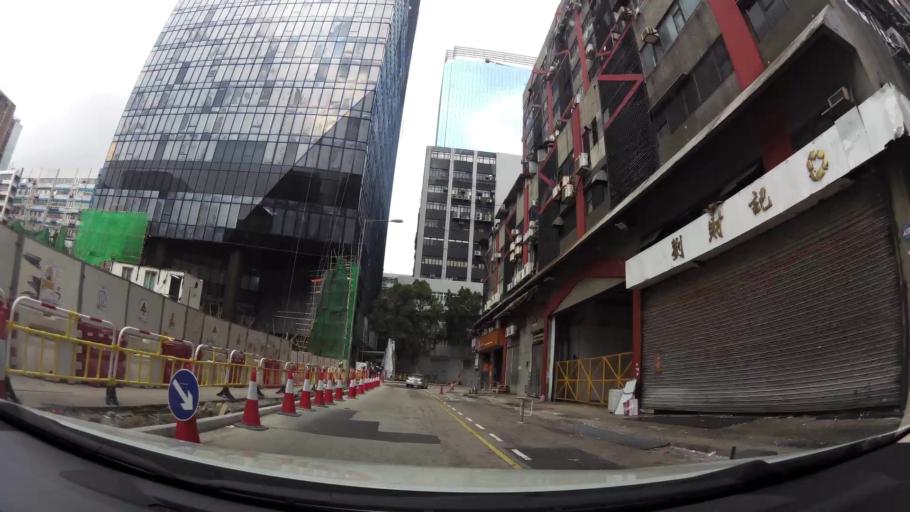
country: HK
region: Kowloon City
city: Kowloon
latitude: 22.3239
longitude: 114.2102
